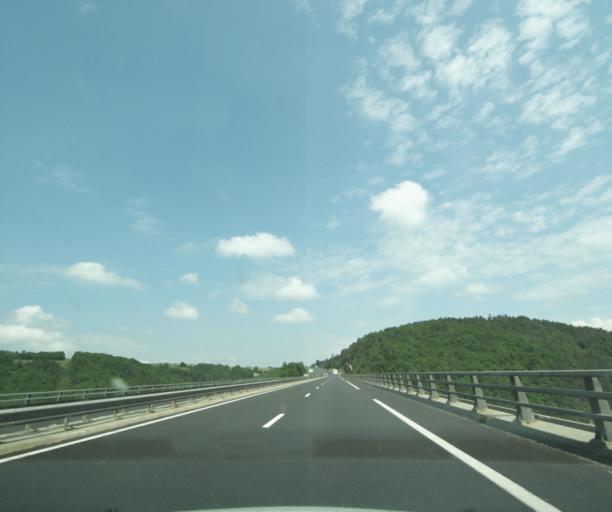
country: FR
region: Auvergne
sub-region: Departement du Cantal
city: Massiac
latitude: 45.2836
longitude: 3.2255
